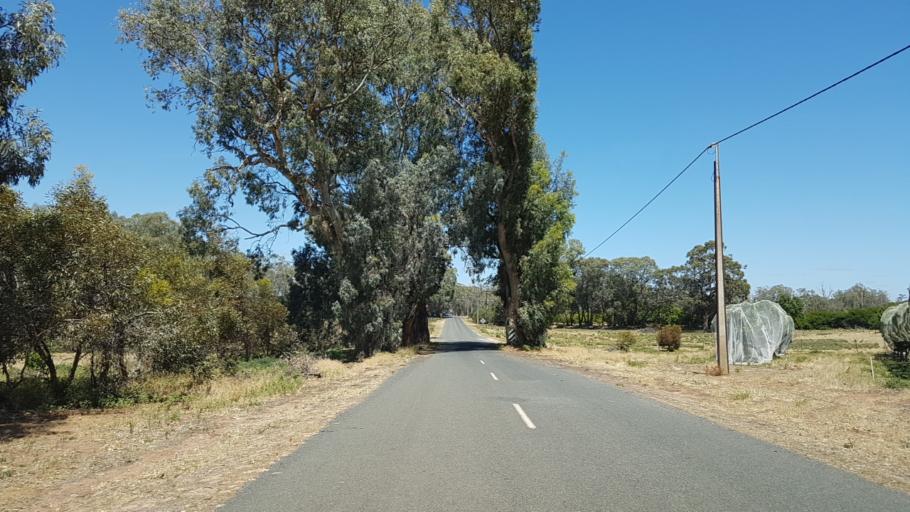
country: AU
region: South Australia
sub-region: Loxton Waikerie
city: Waikerie
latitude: -34.1654
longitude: 140.0289
